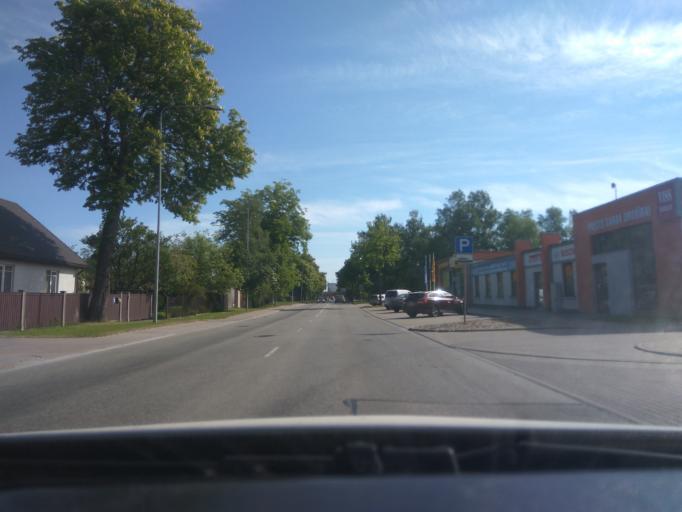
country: LV
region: Ventspils
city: Ventspils
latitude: 57.3823
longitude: 21.5818
